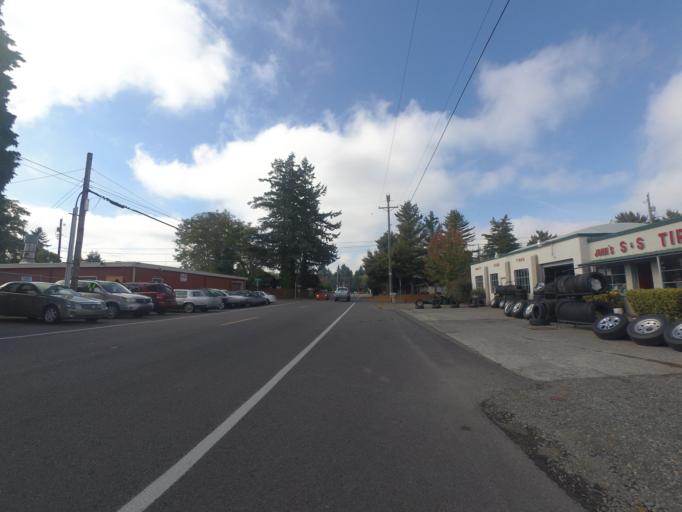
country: US
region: Washington
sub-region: Pierce County
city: Lakewood
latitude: 47.1975
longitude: -122.5055
